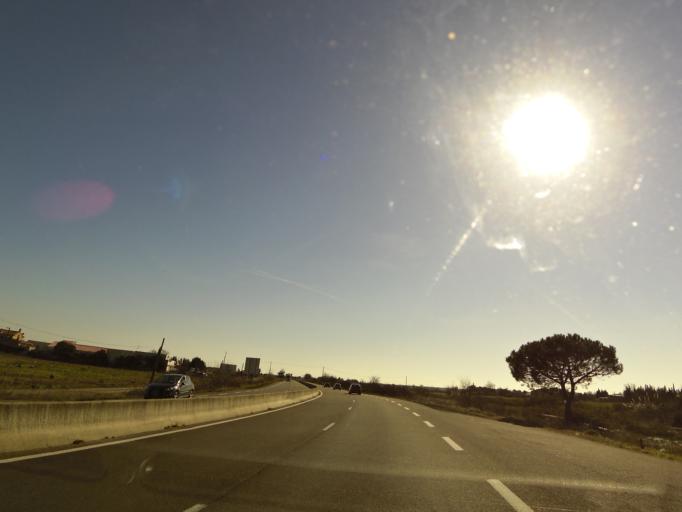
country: FR
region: Languedoc-Roussillon
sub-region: Departement de l'Herault
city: Marsillargues
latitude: 43.6266
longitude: 4.1907
